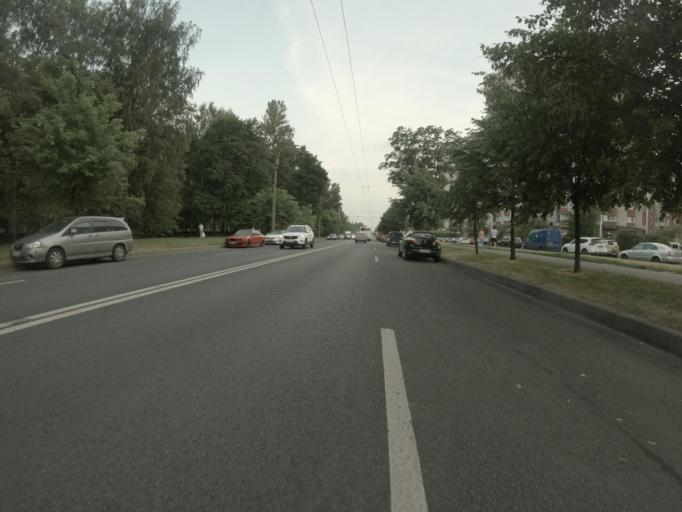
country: RU
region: Leningrad
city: Kalininskiy
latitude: 59.9811
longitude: 30.3962
